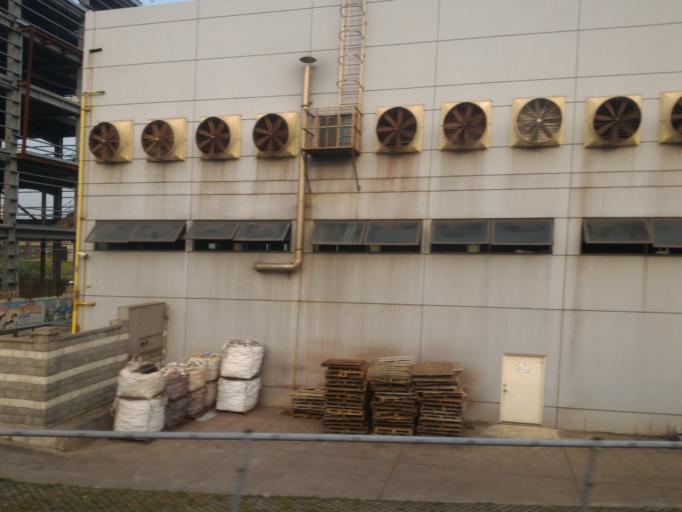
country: TW
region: Taiwan
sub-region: Taoyuan
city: Taoyuan
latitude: 24.9505
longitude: 121.3367
